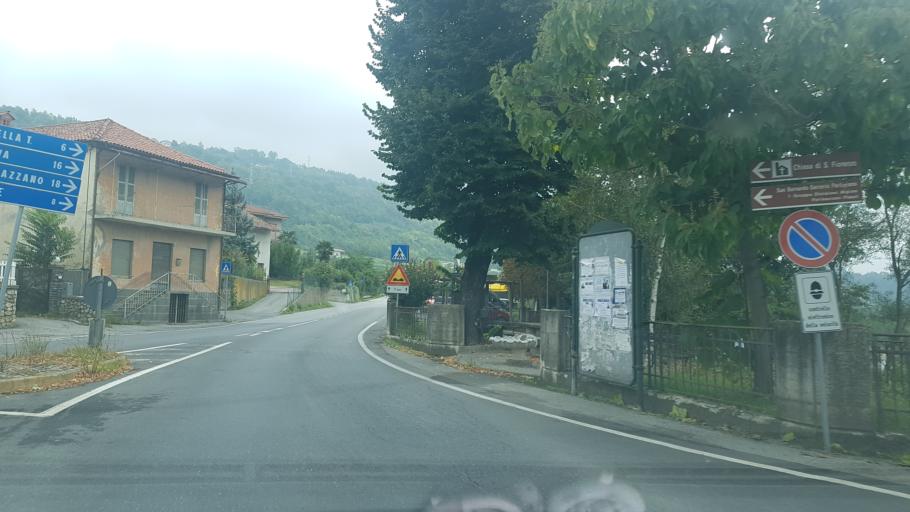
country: IT
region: Piedmont
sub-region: Provincia di Cuneo
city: Bastia Mondovi
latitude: 44.4411
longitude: 7.8939
